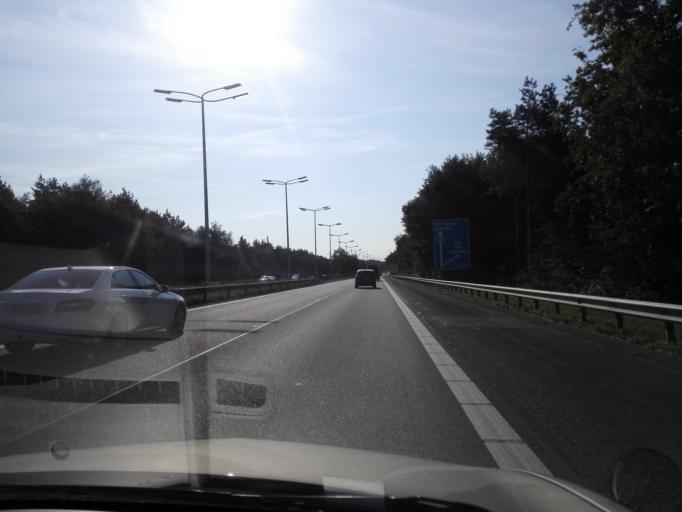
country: BE
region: Flanders
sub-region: Provincie Limburg
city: Genk
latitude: 50.9978
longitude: 5.4805
